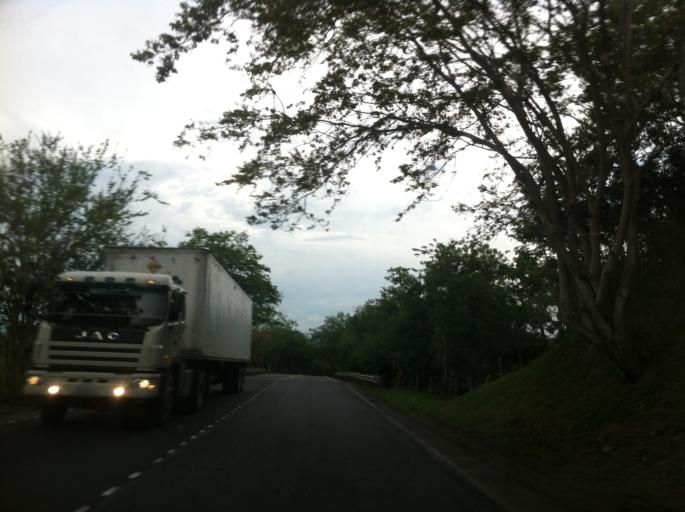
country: CO
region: Valle del Cauca
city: Zarzal
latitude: 4.3519
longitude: -76.0260
